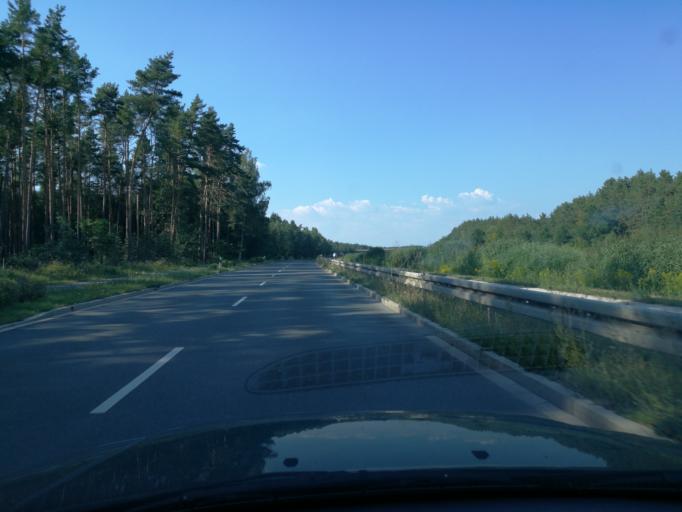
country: DE
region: Bavaria
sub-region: Regierungsbezirk Mittelfranken
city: Mohrendorf
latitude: 49.6093
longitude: 10.9719
